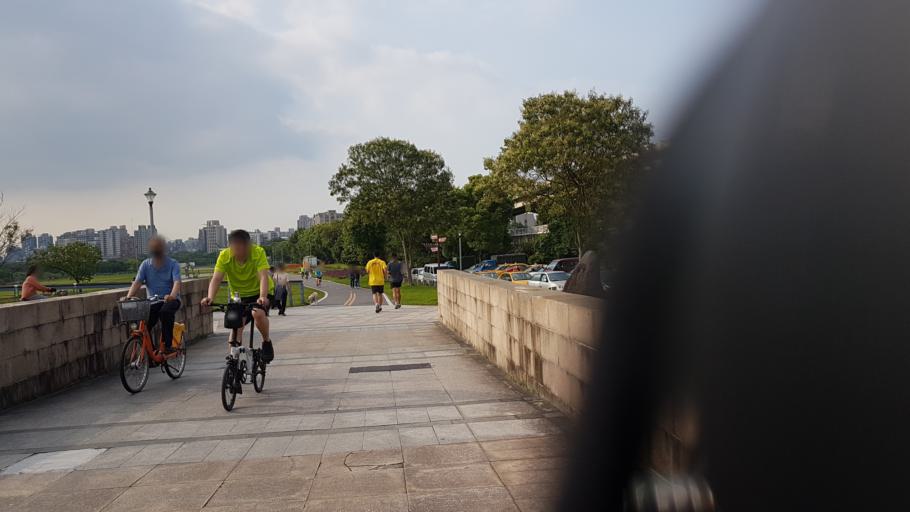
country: TW
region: Taipei
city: Taipei
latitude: 25.0127
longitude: 121.5270
